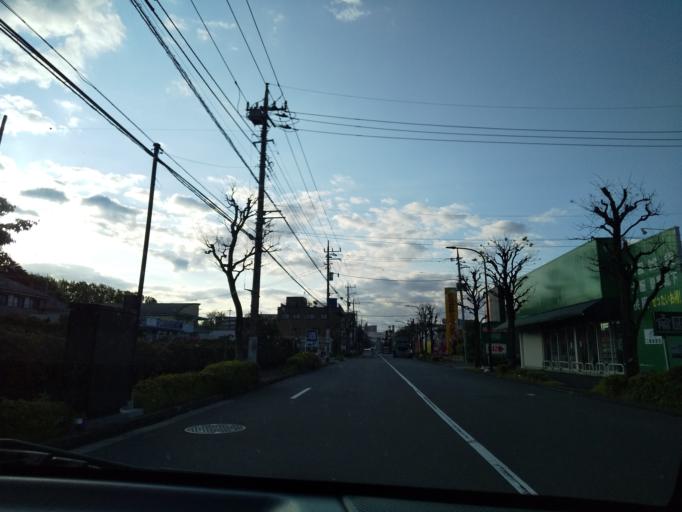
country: JP
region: Tokyo
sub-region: Machida-shi
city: Machida
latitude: 35.5507
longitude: 139.4327
